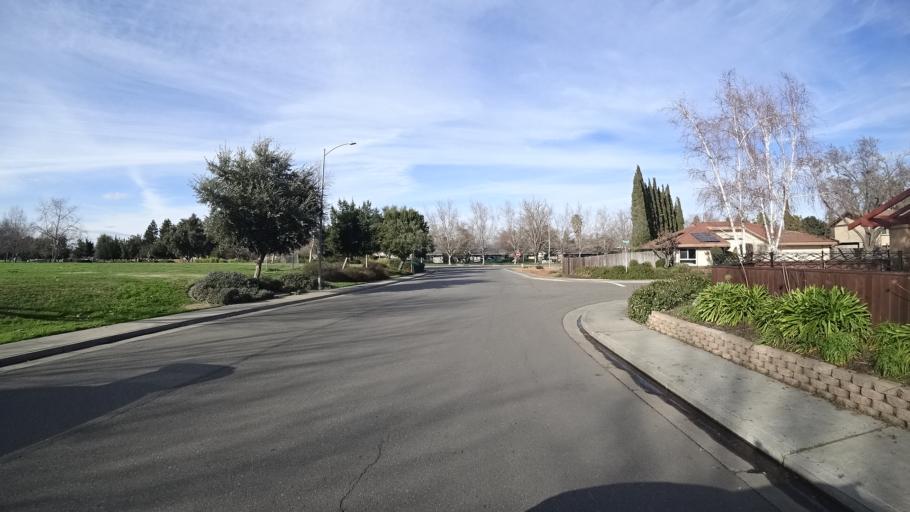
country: US
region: California
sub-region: Yolo County
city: Davis
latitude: 38.5468
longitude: -121.7043
